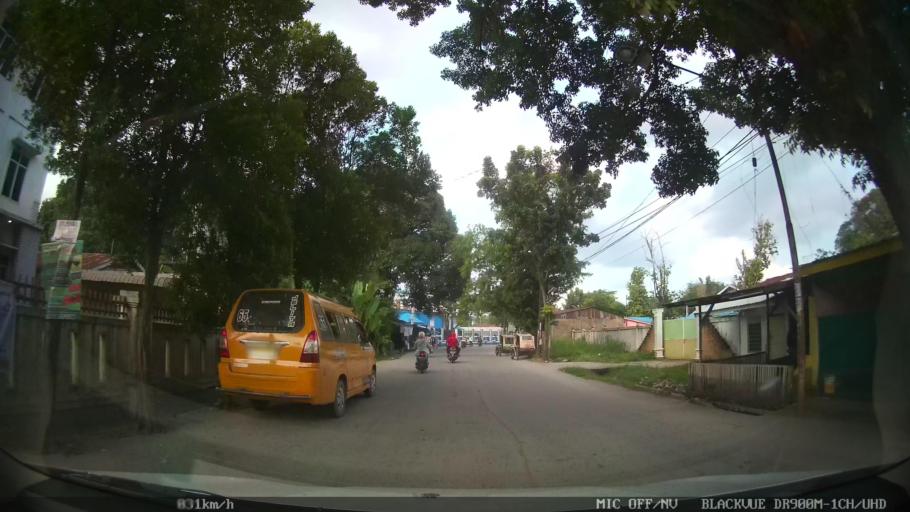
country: ID
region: North Sumatra
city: Medan
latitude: 3.5842
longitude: 98.7321
